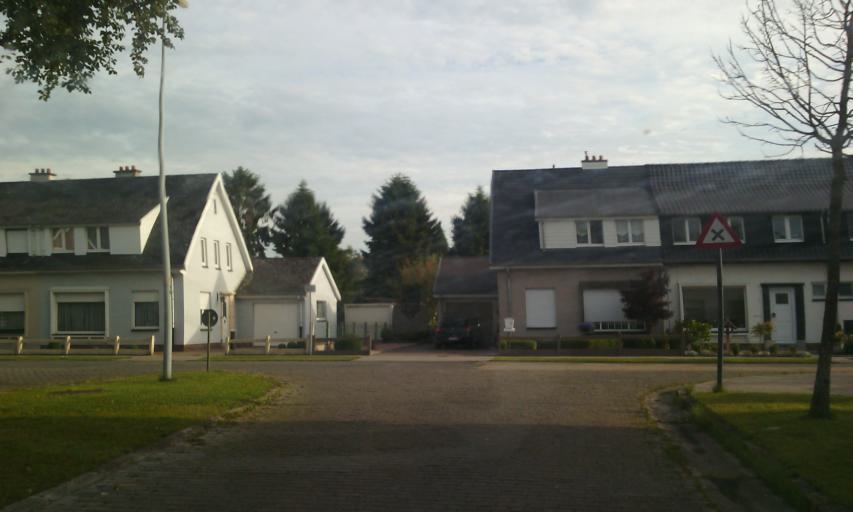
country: BE
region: Flanders
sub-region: Provincie Oost-Vlaanderen
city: Zele
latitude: 51.0740
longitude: 4.0327
